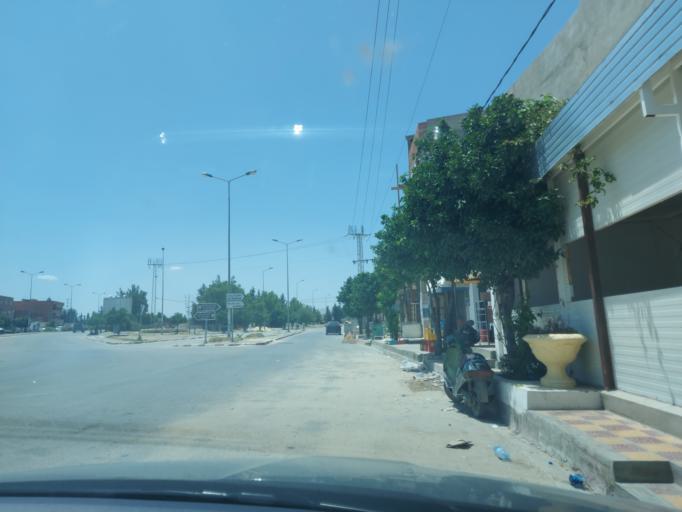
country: TN
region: Silyanah
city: Siliana
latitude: 36.0853
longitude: 9.3557
